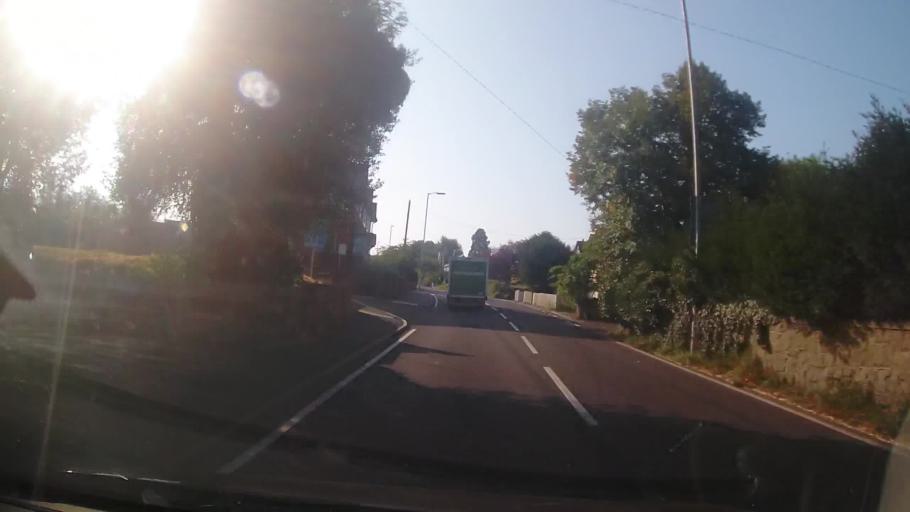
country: GB
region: England
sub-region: Shropshire
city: Harley
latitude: 52.6323
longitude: -2.6044
